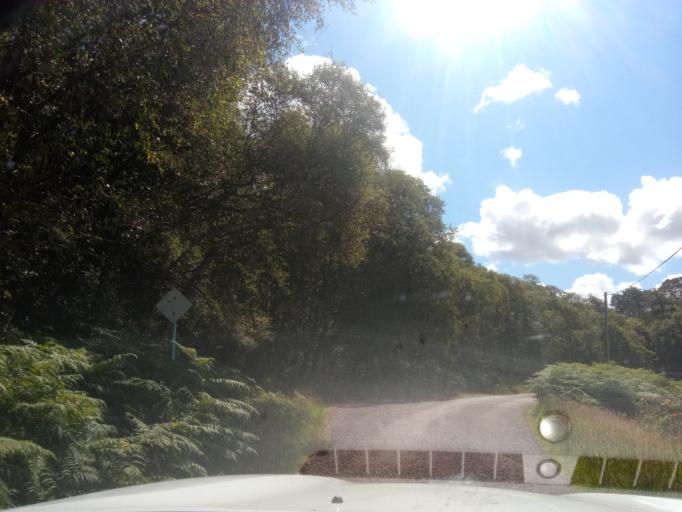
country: GB
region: Scotland
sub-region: Argyll and Bute
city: Isle Of Mull
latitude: 56.7588
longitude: -5.8127
